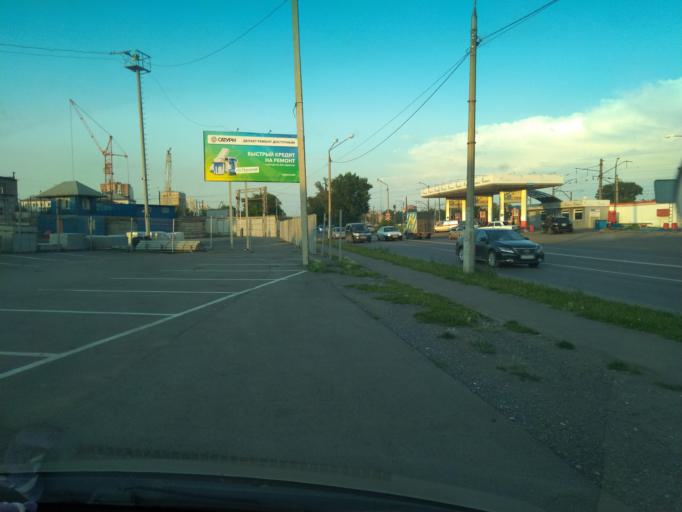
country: RU
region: Krasnoyarskiy
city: Krasnoyarsk
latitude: 55.9924
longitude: 92.9222
